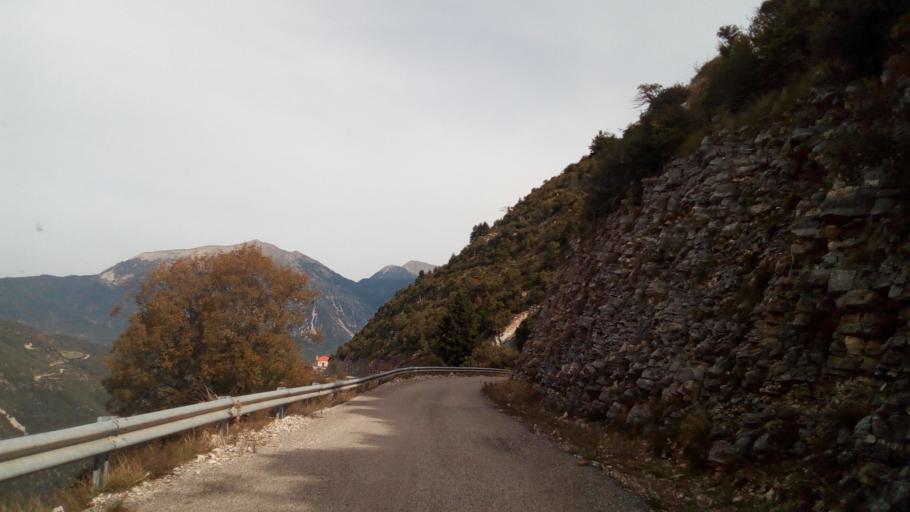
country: GR
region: West Greece
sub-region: Nomos Aitolias kai Akarnanias
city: Thermo
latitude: 38.5705
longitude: 21.8183
